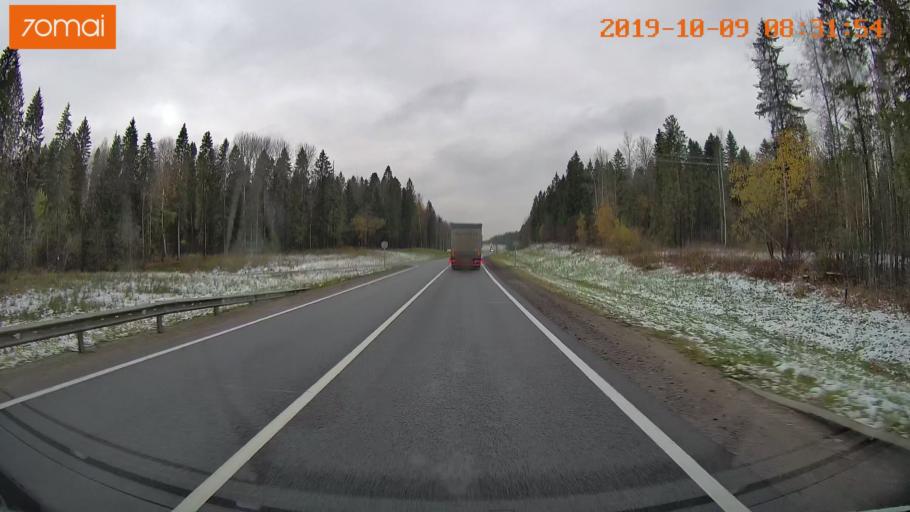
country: RU
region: Vologda
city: Gryazovets
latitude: 58.8598
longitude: 40.1992
